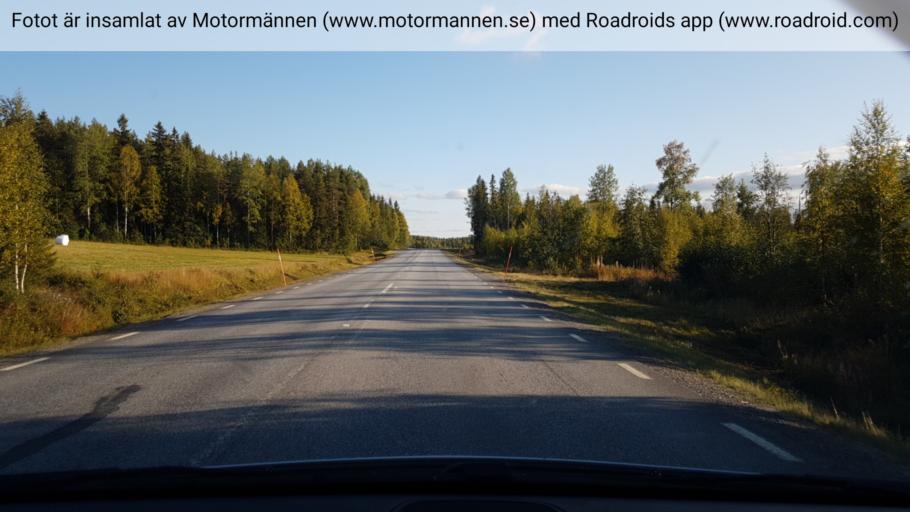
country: SE
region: Vaesterbotten
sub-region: Vannas Kommun
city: Vaennaes
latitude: 63.9323
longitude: 19.7715
